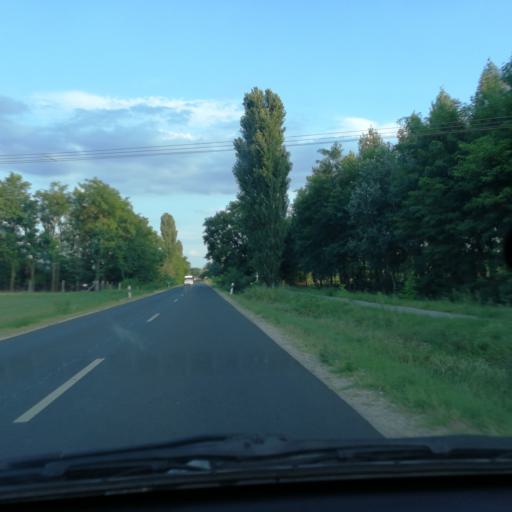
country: HU
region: Bacs-Kiskun
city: Jaszszentlaszlo
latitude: 46.5312
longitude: 19.7404
